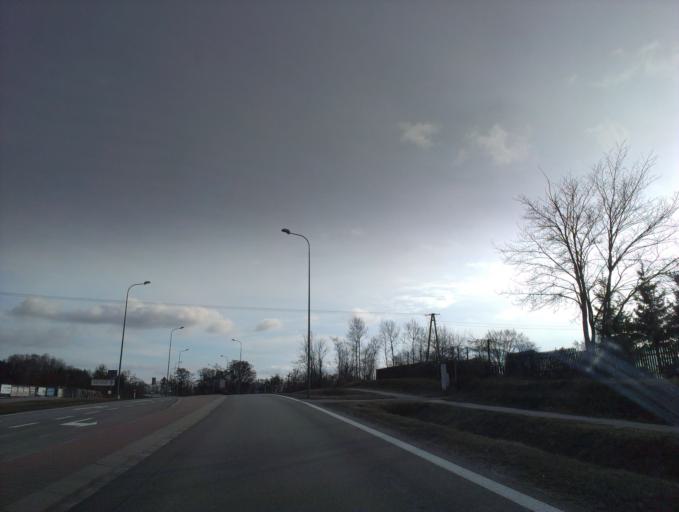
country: PL
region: Kujawsko-Pomorskie
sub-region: Powiat lipnowski
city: Lipno
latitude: 52.8592
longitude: 19.1573
